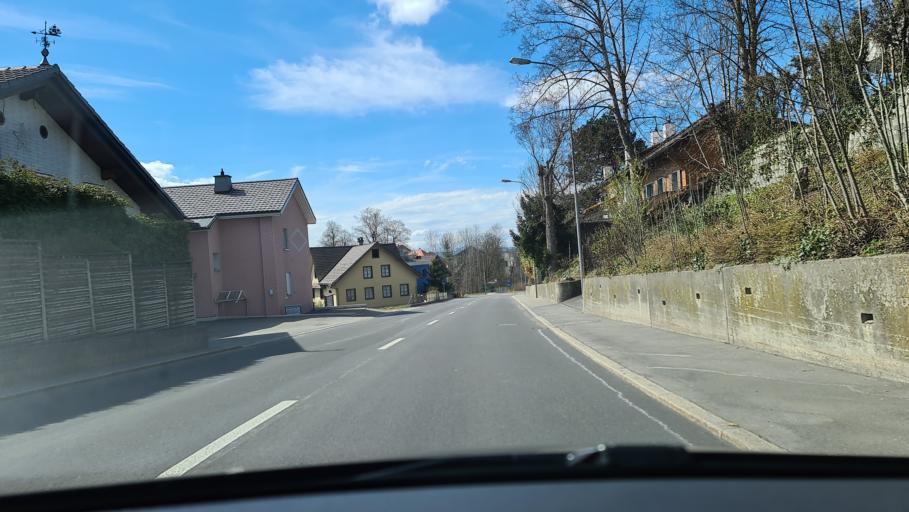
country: CH
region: Zug
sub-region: Zug
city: Menzingen
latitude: 47.1810
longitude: 8.5752
